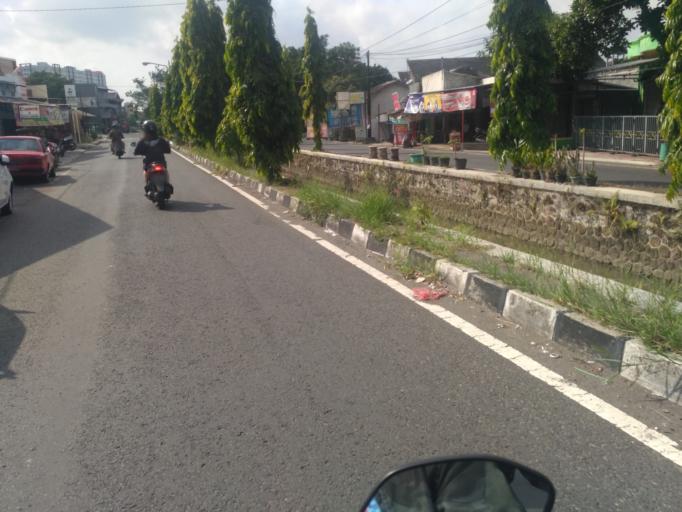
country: ID
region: Daerah Istimewa Yogyakarta
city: Yogyakarta
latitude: -7.7619
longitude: 110.3672
